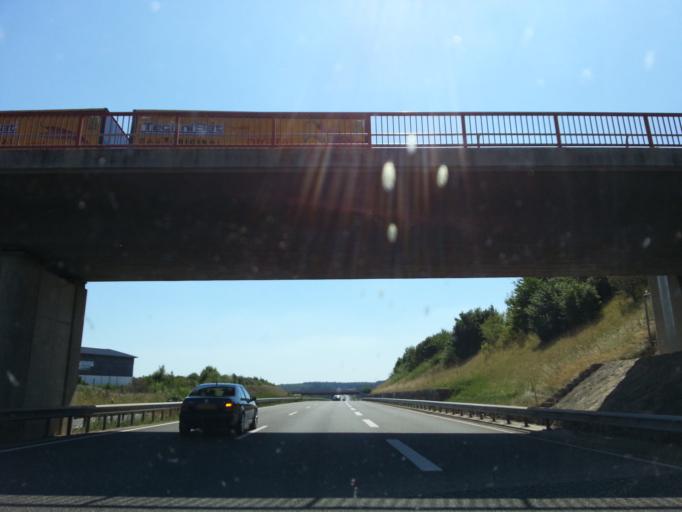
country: DE
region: Rheinland-Pfalz
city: Landscheid
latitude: 49.9924
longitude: 6.7790
